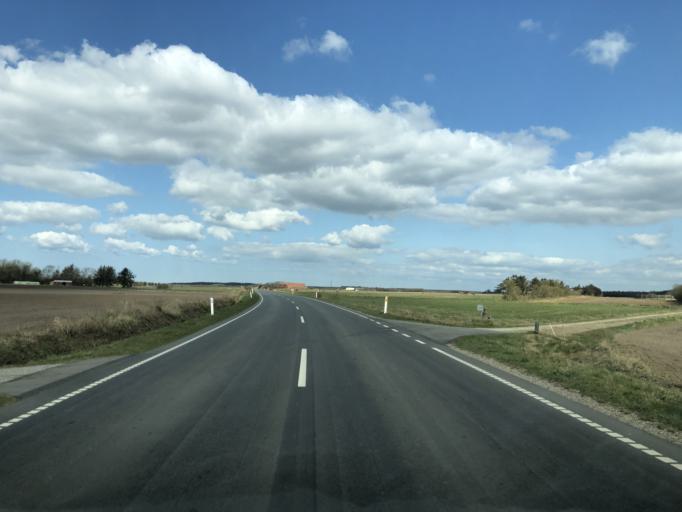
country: DK
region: Central Jutland
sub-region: Lemvig Kommune
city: Lemvig
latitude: 56.4283
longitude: 8.3038
